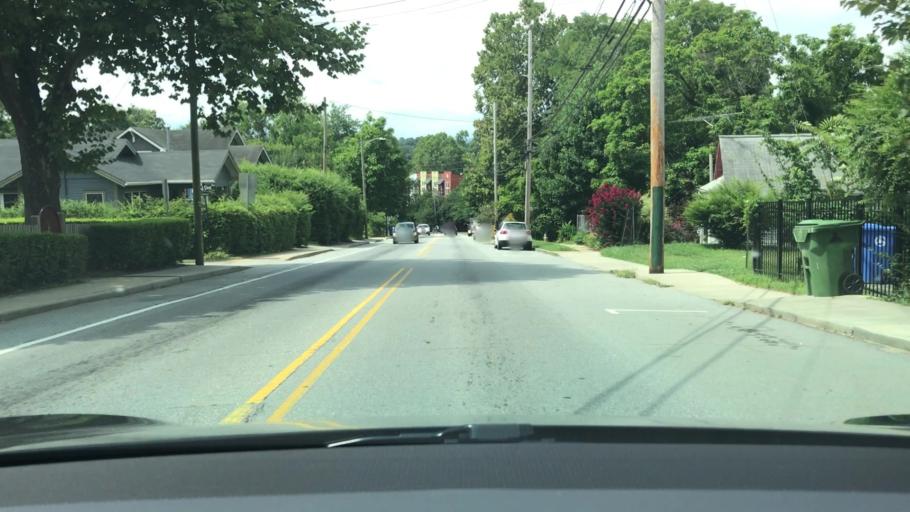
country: US
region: North Carolina
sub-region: Buncombe County
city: Asheville
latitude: 35.5903
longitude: -82.5629
